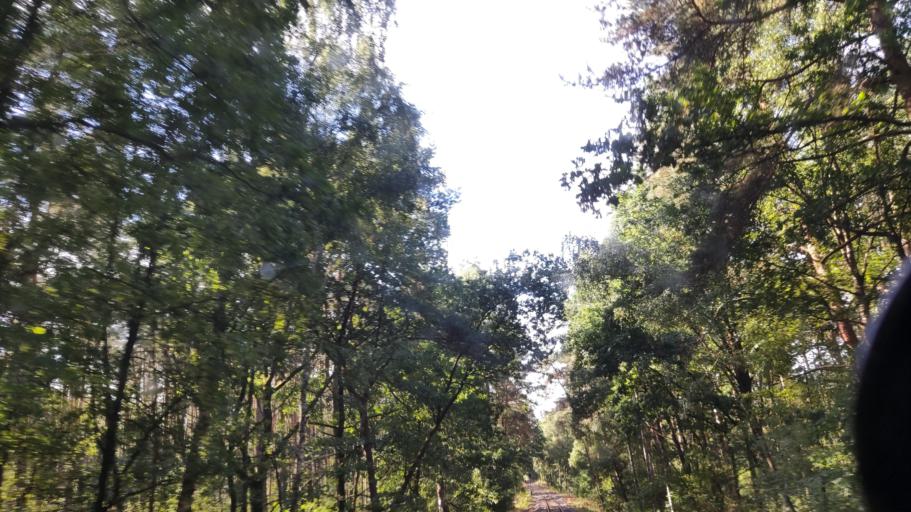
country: DE
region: Lower Saxony
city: Soltau
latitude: 53.0108
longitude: 9.8903
